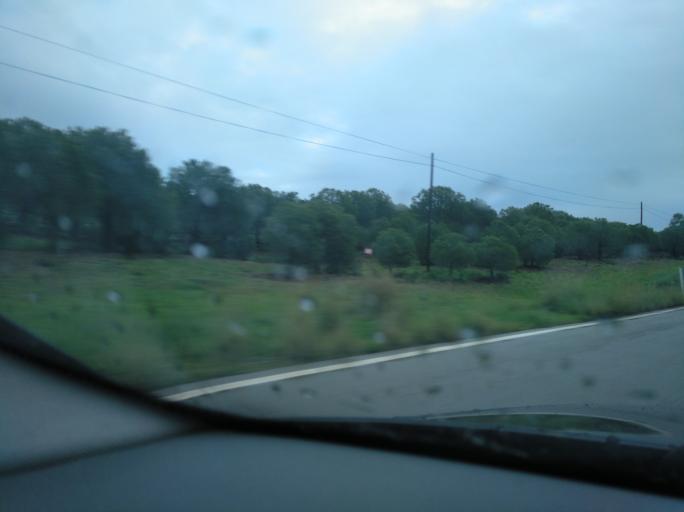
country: PT
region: Beja
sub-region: Mertola
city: Mertola
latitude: 37.5318
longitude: -7.6163
